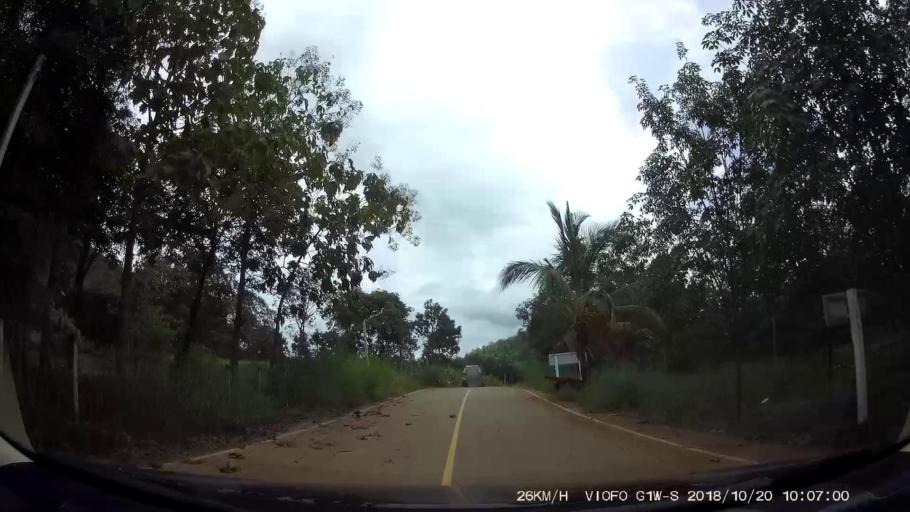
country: TH
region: Chaiyaphum
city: Khon San
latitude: 16.5465
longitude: 101.8522
